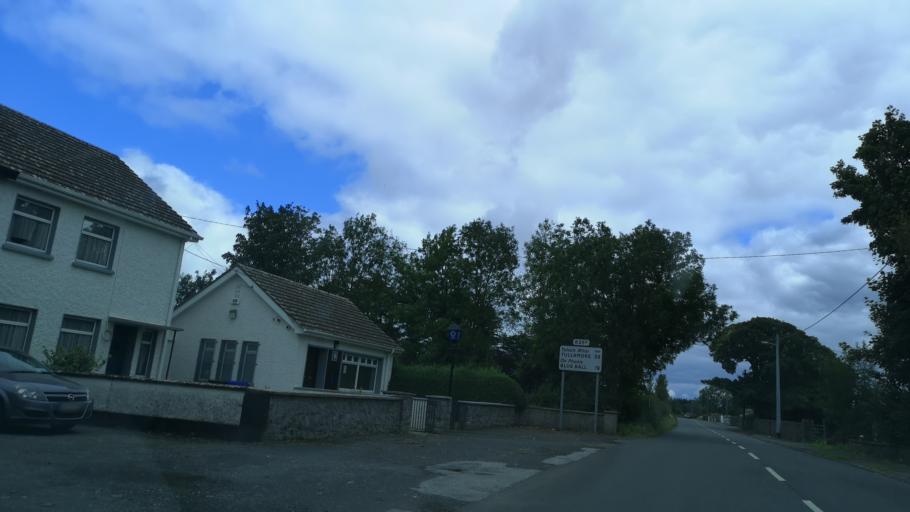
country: IE
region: Leinster
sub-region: Uibh Fhaili
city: Ferbane
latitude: 53.2247
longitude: -7.8780
